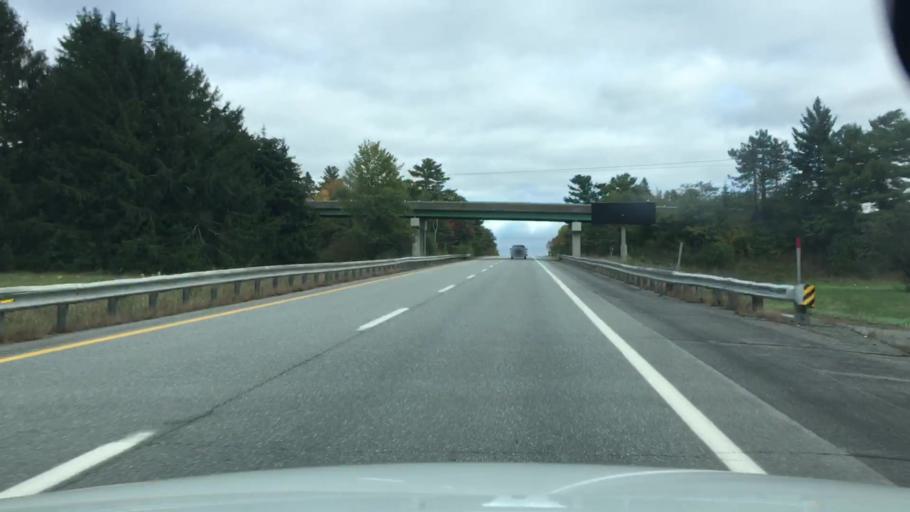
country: US
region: Maine
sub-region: Penobscot County
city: Carmel
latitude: 44.7783
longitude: -69.0632
